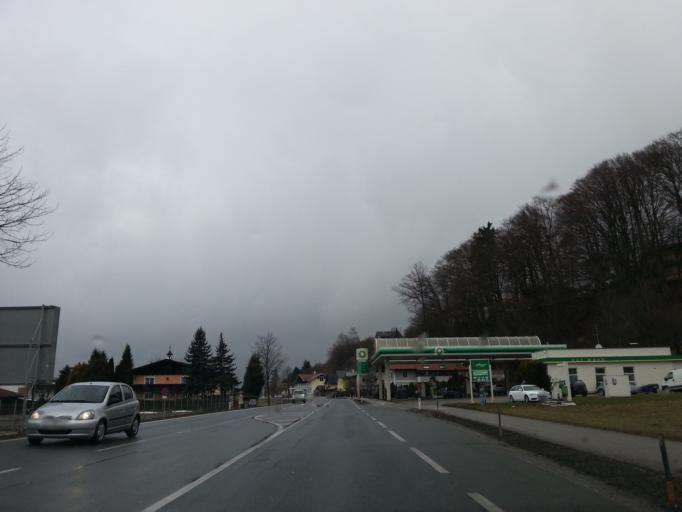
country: AT
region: Salzburg
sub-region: Politischer Bezirk Salzburg-Umgebung
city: Strasswalchen
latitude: 47.9874
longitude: 13.2499
